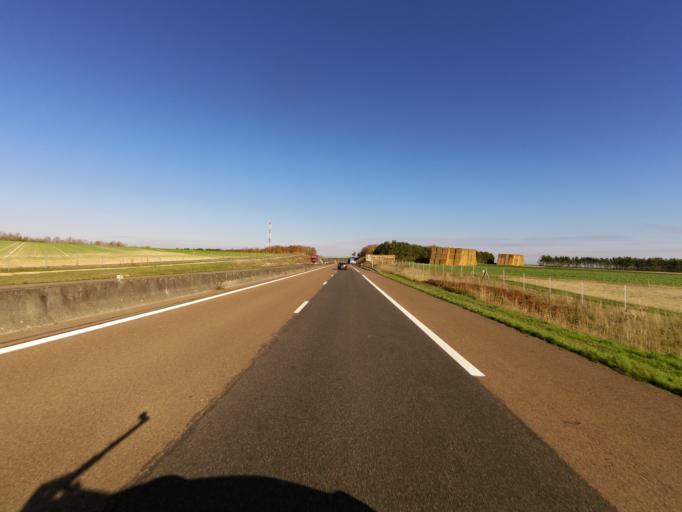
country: FR
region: Champagne-Ardenne
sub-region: Departement de la Marne
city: Compertrix
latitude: 48.8752
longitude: 4.2893
